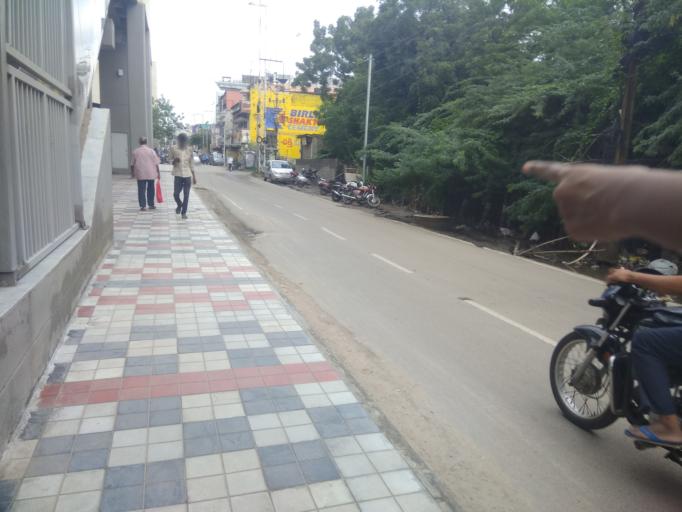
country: IN
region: Telangana
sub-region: Rangareddi
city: Gaddi Annaram
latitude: 17.3685
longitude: 78.5347
